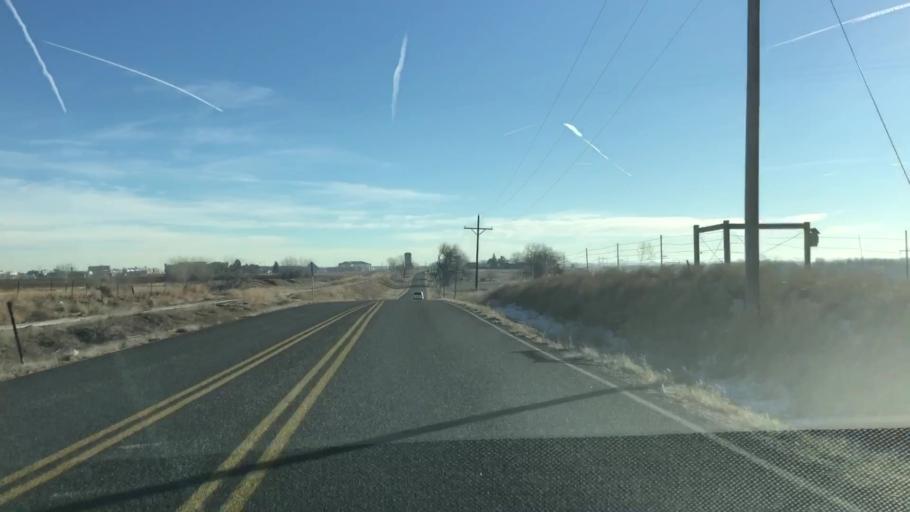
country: US
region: Colorado
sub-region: Larimer County
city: Loveland
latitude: 40.3998
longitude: -105.0036
